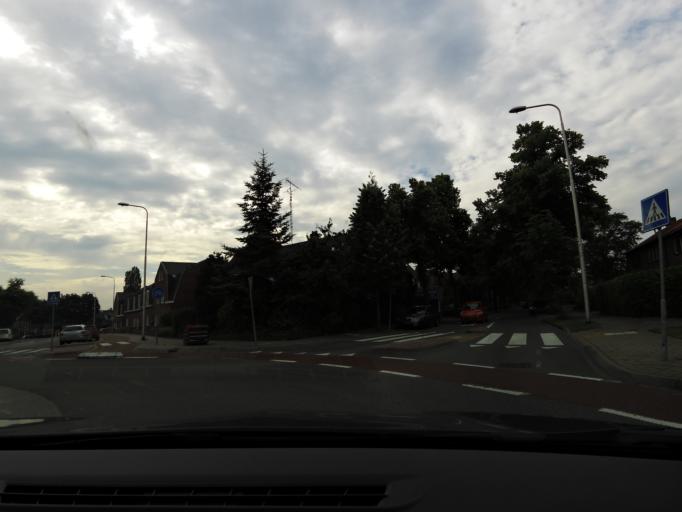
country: NL
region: Gelderland
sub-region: Gemeente Rozendaal
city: Rozendaal
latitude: 52.0006
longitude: 5.9615
